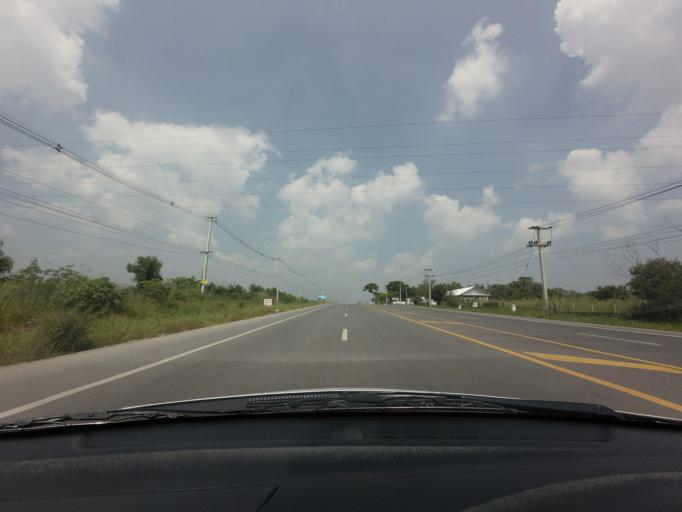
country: TH
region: Nakhon Ratchasima
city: Pak Chong
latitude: 14.6642
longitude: 101.4592
